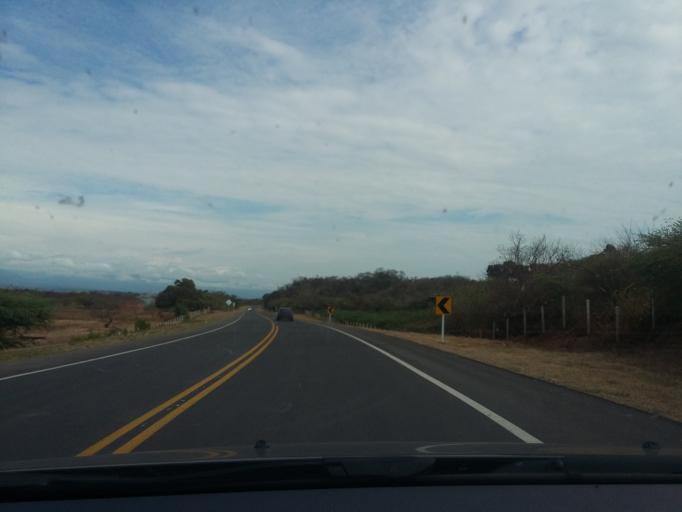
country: CO
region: Tolima
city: Ambalema
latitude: 4.6701
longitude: -74.7816
